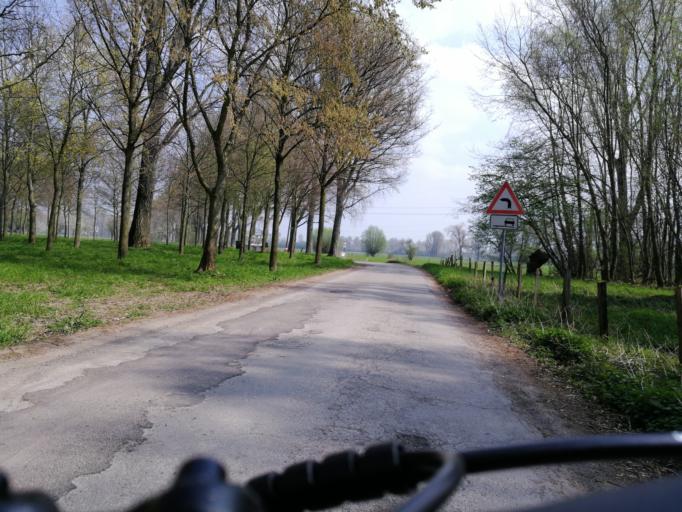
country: DE
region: North Rhine-Westphalia
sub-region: Regierungsbezirk Dusseldorf
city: Dormagen
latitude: 51.1439
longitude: 6.8249
